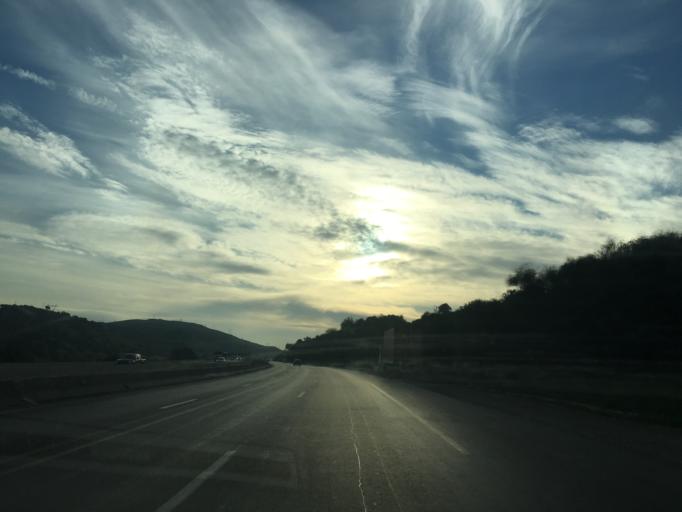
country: DZ
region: Bouira
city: Draa el Mizan
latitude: 36.4605
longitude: 3.7719
